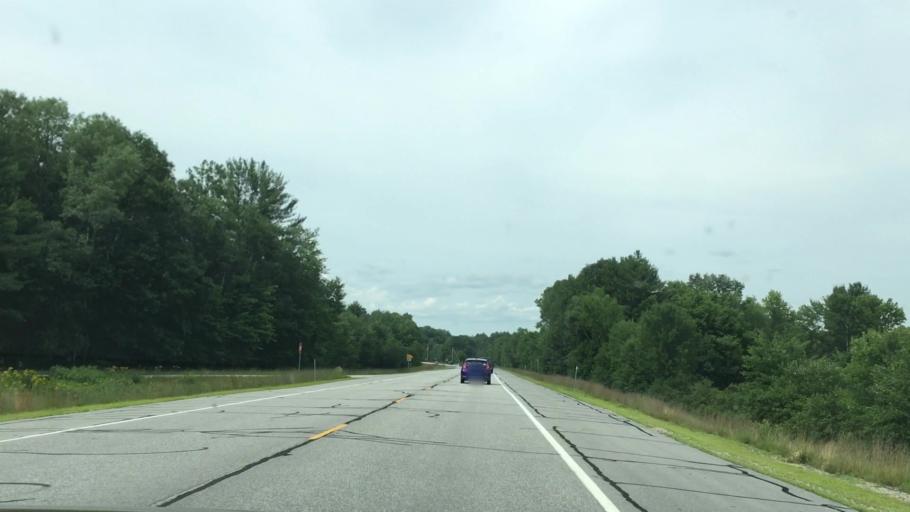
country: US
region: New Hampshire
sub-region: Hillsborough County
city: Hillsborough
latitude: 43.0805
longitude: -71.9172
